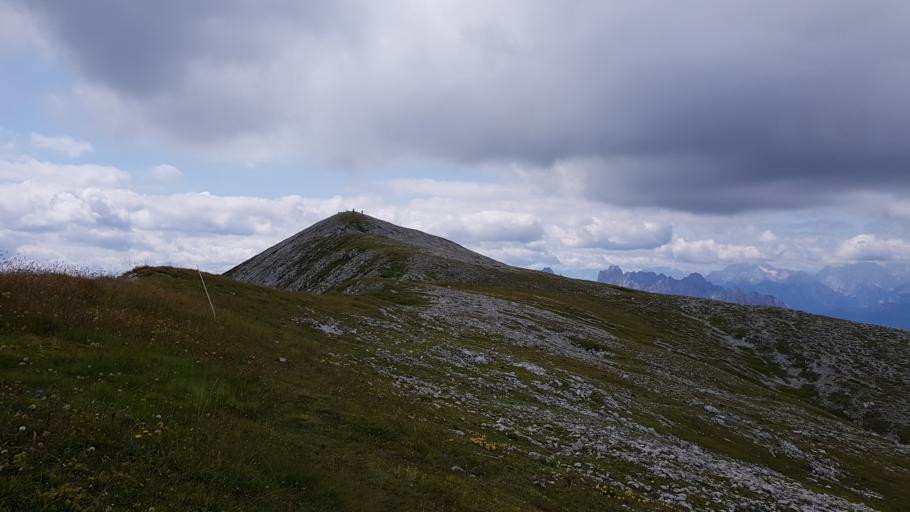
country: IT
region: Friuli Venezia Giulia
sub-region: Provincia di Udine
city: Vico
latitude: 46.4388
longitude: 12.6342
